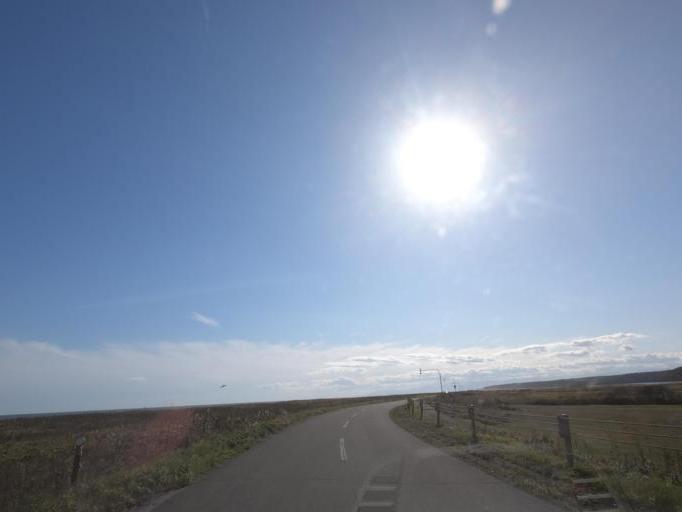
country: JP
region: Hokkaido
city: Obihiro
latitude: 42.6002
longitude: 143.5497
